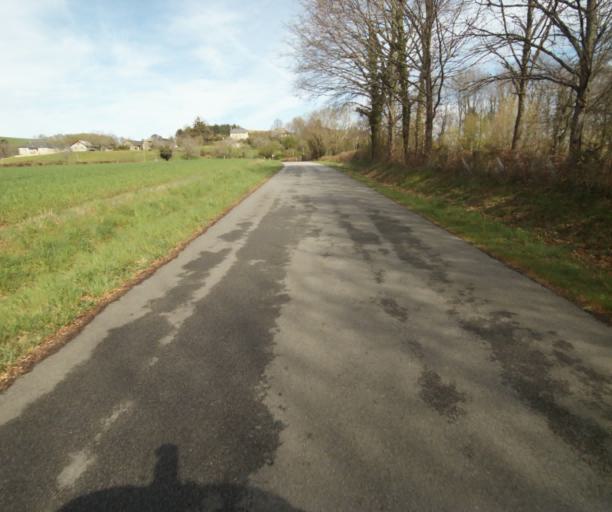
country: FR
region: Limousin
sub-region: Departement de la Correze
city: Laguenne
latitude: 45.2672
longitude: 1.8164
